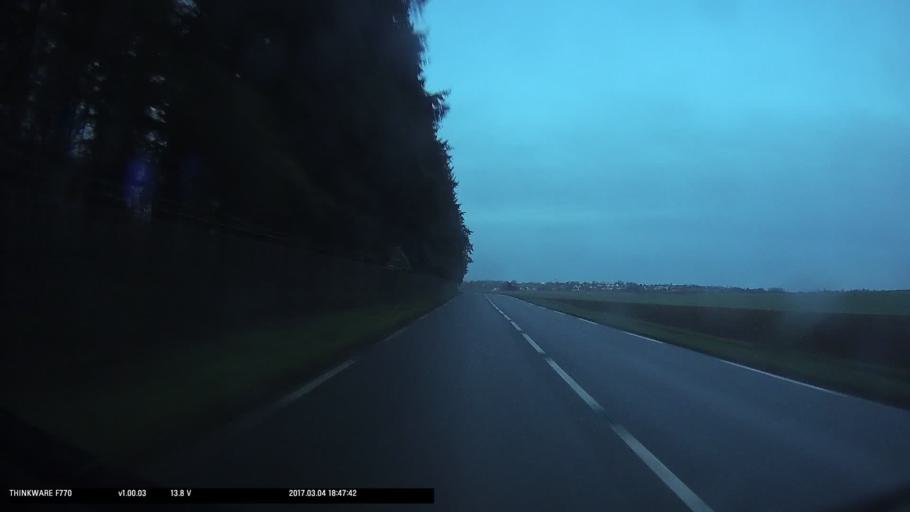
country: FR
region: Ile-de-France
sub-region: Departement du Val-d'Oise
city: Us
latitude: 49.1118
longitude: 1.9791
